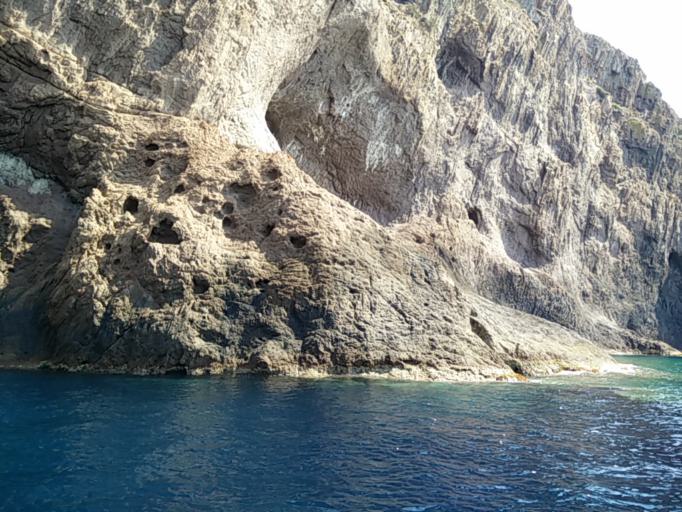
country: FR
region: Corsica
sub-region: Departement de la Corse-du-Sud
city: Cargese
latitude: 42.3452
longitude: 8.5533
